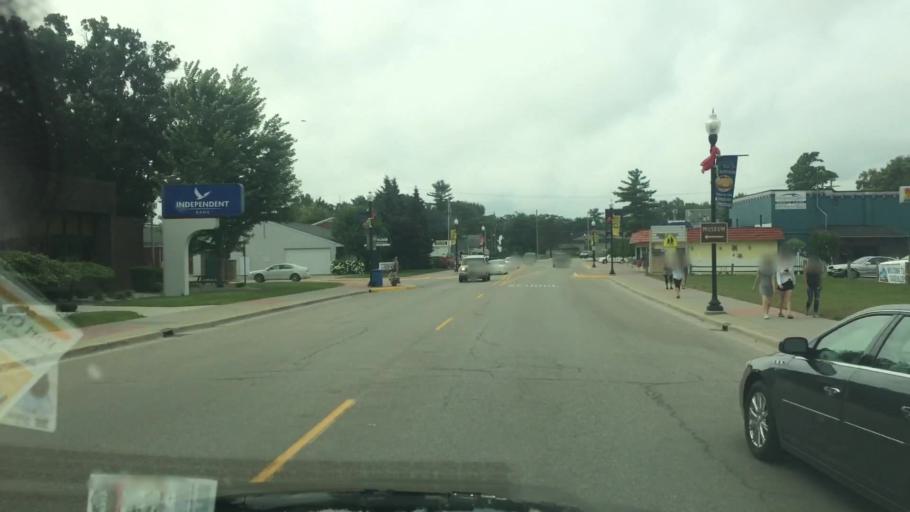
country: US
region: Michigan
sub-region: Huron County
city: Pigeon
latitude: 43.9399
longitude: -83.2724
